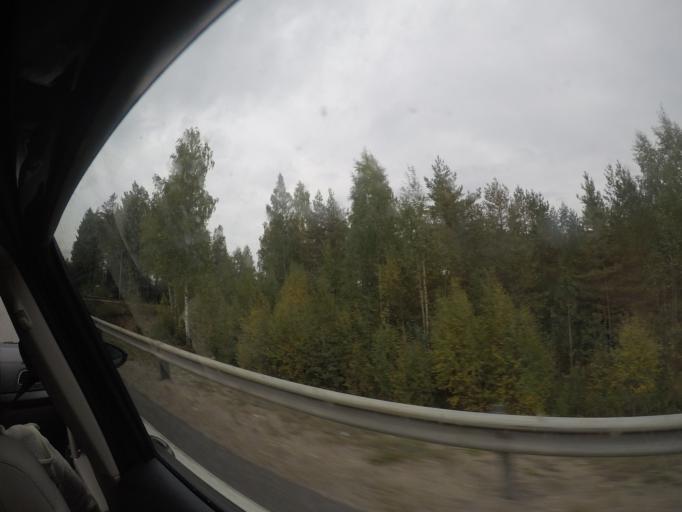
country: FI
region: Pirkanmaa
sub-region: Ylae-Pirkanmaa
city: Juupajoki
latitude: 61.7675
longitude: 24.3077
